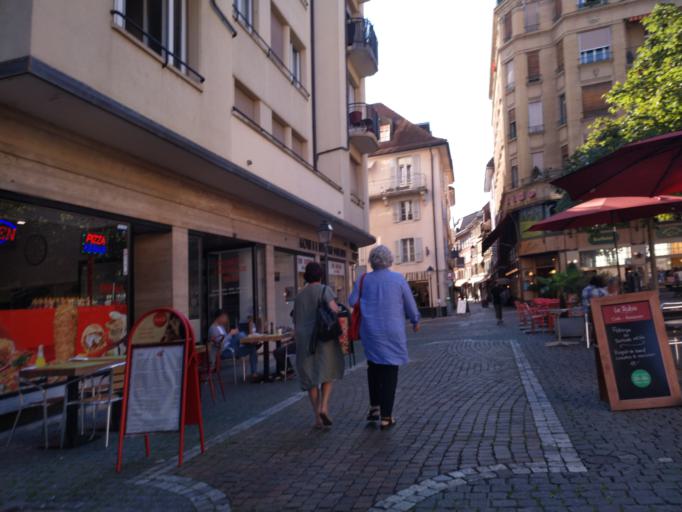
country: CH
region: Vaud
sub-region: Riviera-Pays-d'Enhaut District
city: Vevey
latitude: 46.4589
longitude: 6.8466
